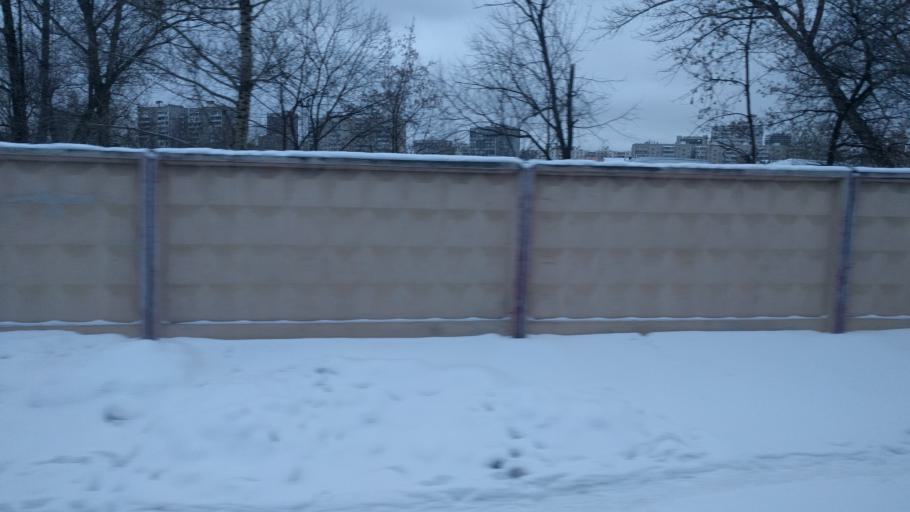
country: RU
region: Moscow
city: Sokol'niki
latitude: 55.7829
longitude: 37.6505
